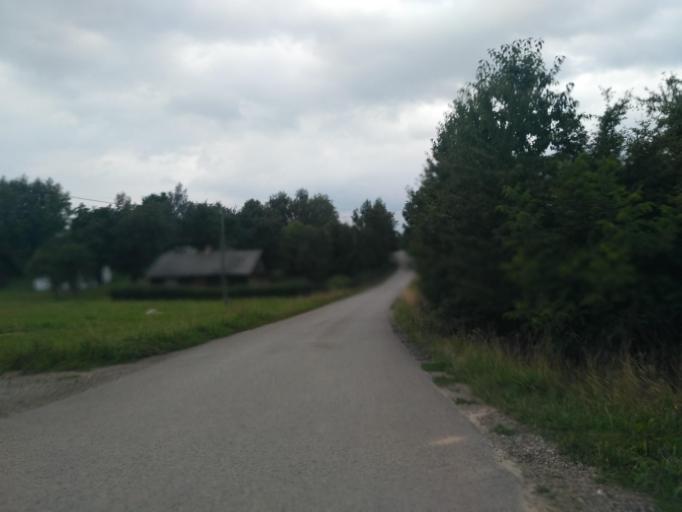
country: PL
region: Subcarpathian Voivodeship
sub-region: Powiat rzeszowski
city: Tyczyn
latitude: 49.9633
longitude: 22.0049
